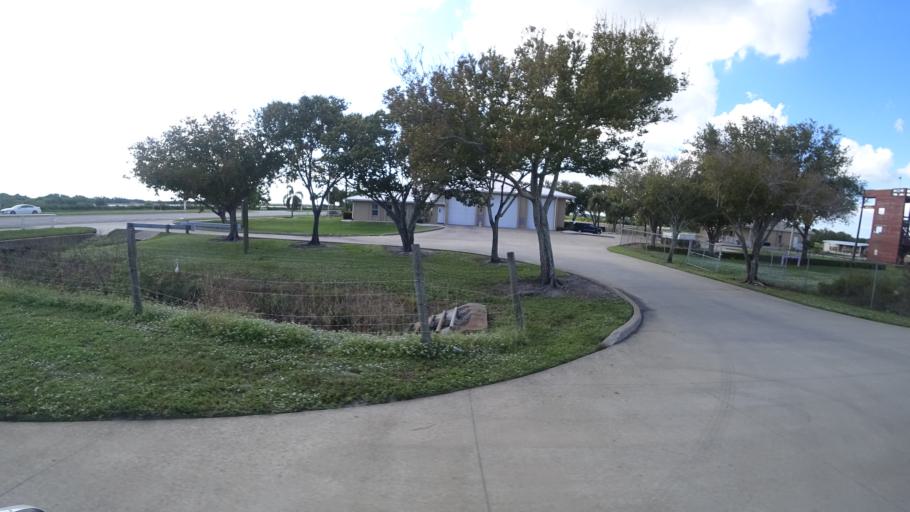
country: US
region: Florida
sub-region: Manatee County
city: Bayshore Gardens
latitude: 27.4484
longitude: -82.6286
